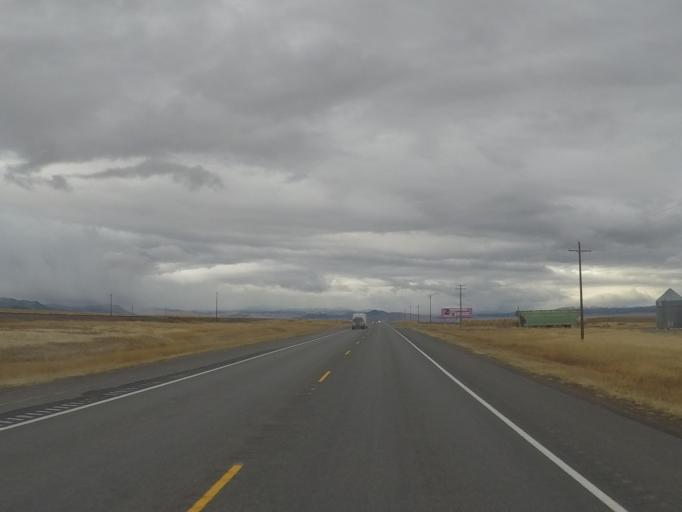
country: US
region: Montana
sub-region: Lewis and Clark County
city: East Helena
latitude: 46.5723
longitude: -111.8267
